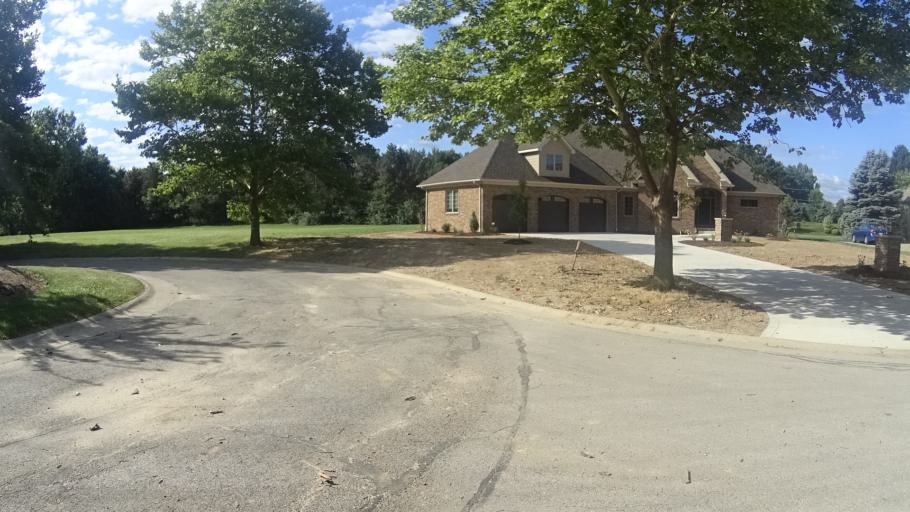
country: US
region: Ohio
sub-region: Erie County
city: Sandusky
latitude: 41.4136
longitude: -82.6583
